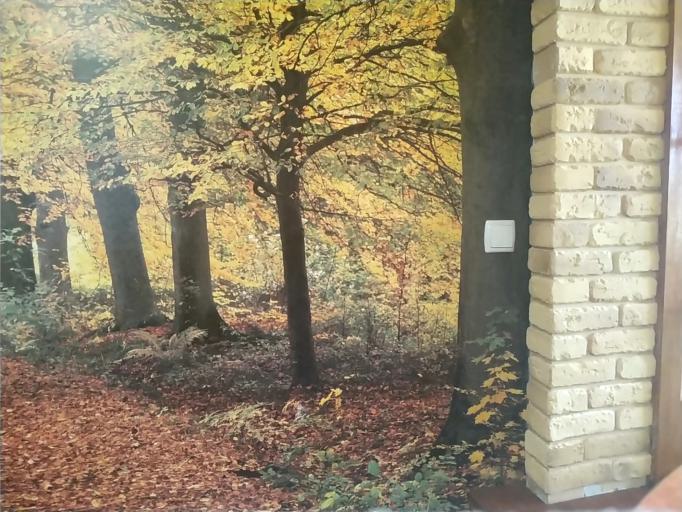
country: RU
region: Tverskaya
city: Vyshniy Volochek
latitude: 57.6717
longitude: 34.5279
